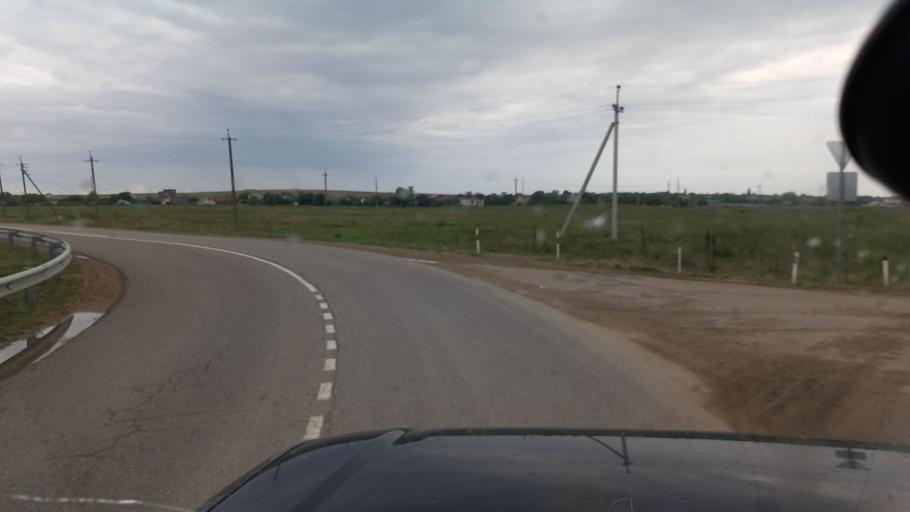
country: RU
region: Krasnodarskiy
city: Akhtanizovskaya
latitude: 45.3377
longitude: 37.1153
